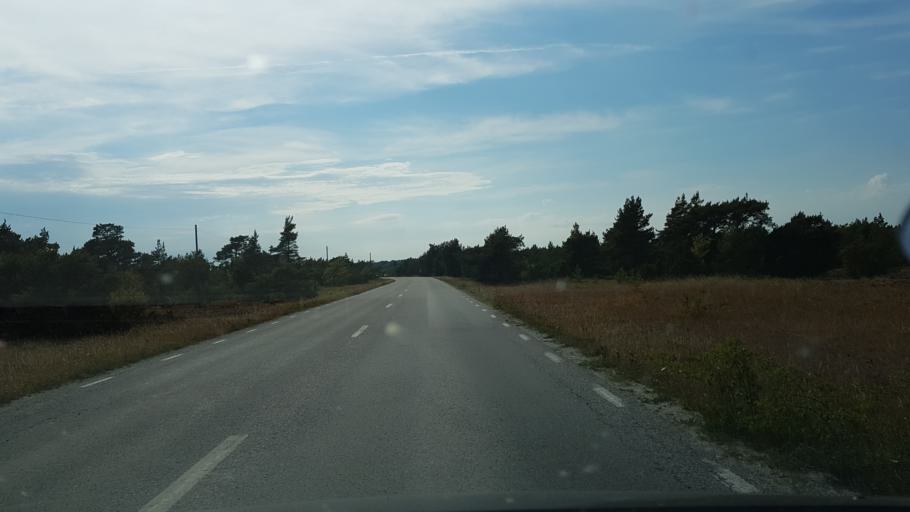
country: SE
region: Gotland
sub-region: Gotland
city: Visby
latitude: 57.6384
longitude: 18.3803
